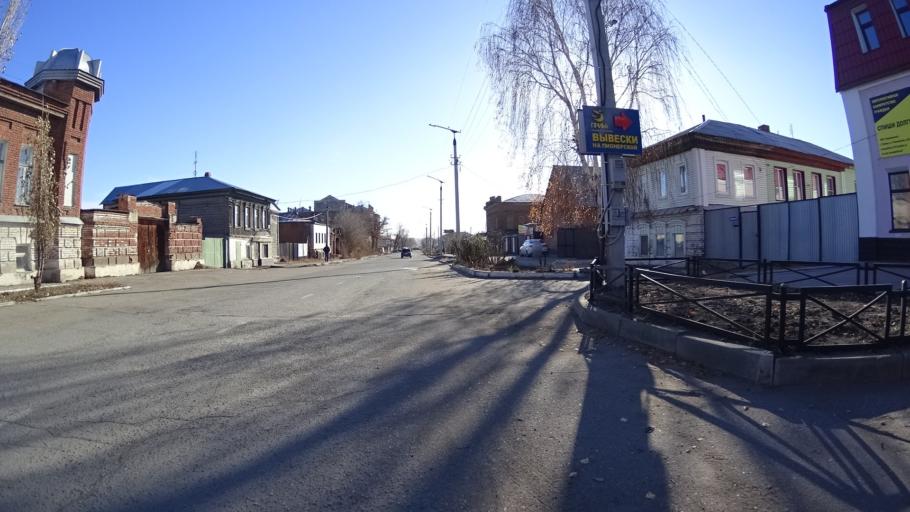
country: RU
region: Chelyabinsk
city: Troitsk
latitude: 54.0834
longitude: 61.5477
